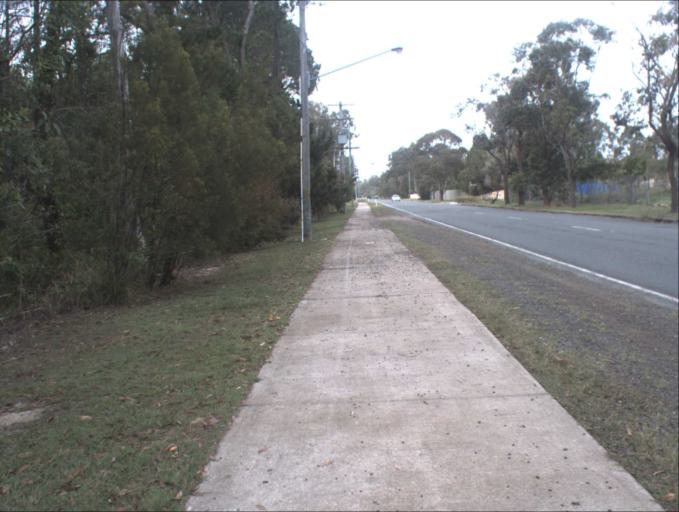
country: AU
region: Queensland
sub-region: Logan
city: Logan Reserve
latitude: -27.7002
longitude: 153.0766
